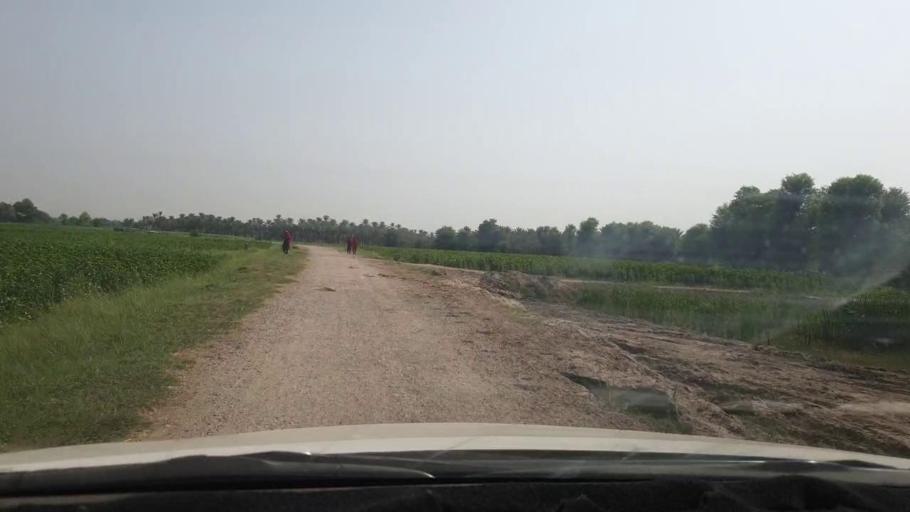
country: PK
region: Sindh
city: Rohri
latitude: 27.6086
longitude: 68.8918
